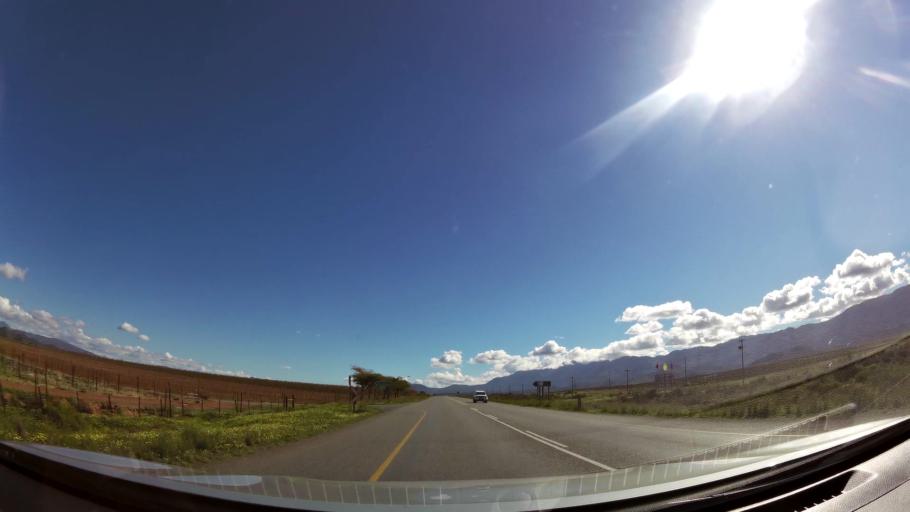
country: ZA
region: Western Cape
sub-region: Cape Winelands District Municipality
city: Ashton
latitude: -33.8374
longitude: 20.0061
